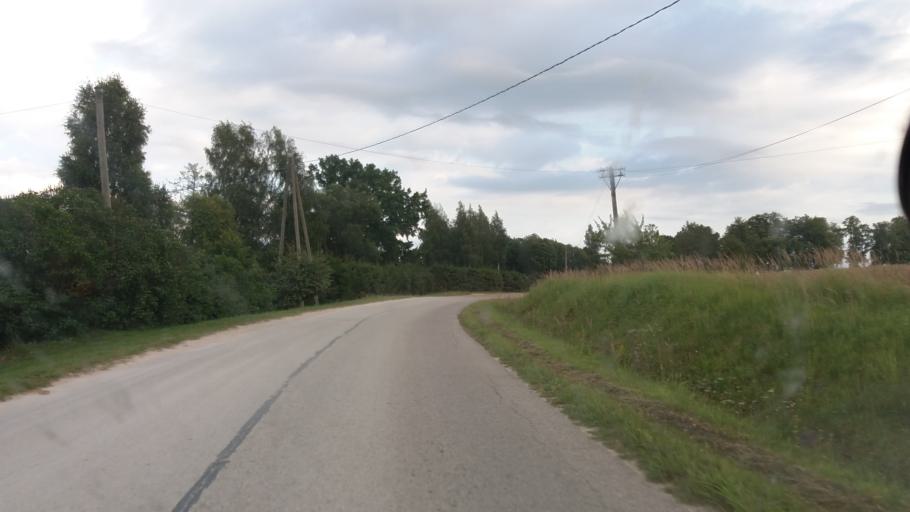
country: LV
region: Talsu Rajons
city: Sabile
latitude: 57.0370
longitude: 22.5718
